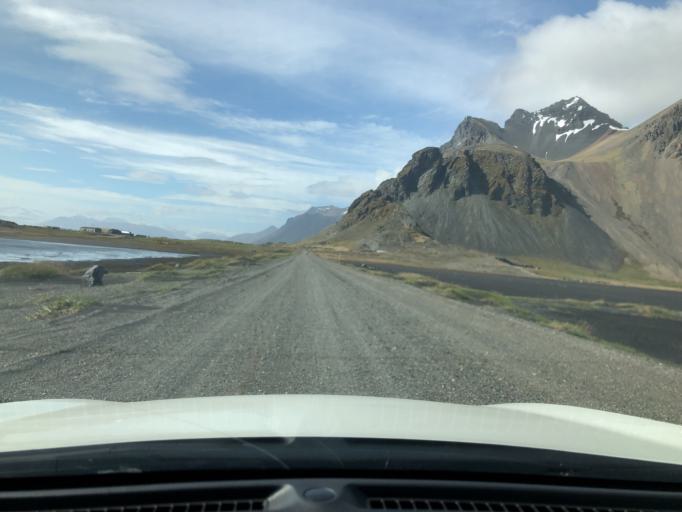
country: IS
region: East
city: Hoefn
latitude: 64.2500
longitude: -14.9846
